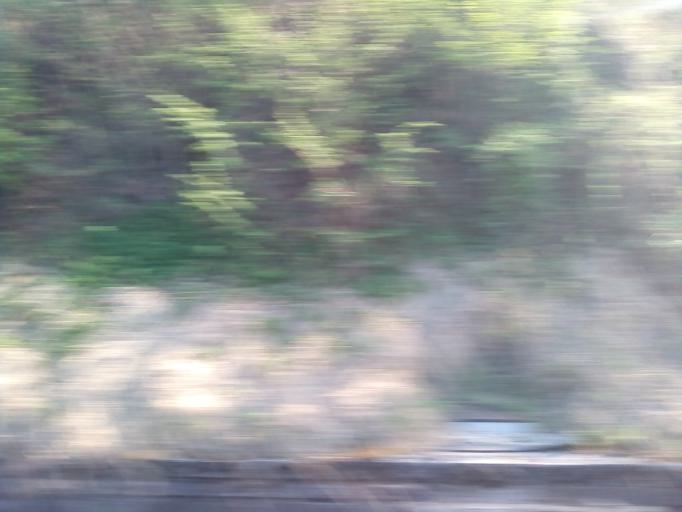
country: FR
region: Rhone-Alpes
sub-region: Departement de l'Isere
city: La Tour-du-Pin
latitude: 45.5623
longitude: 5.4411
